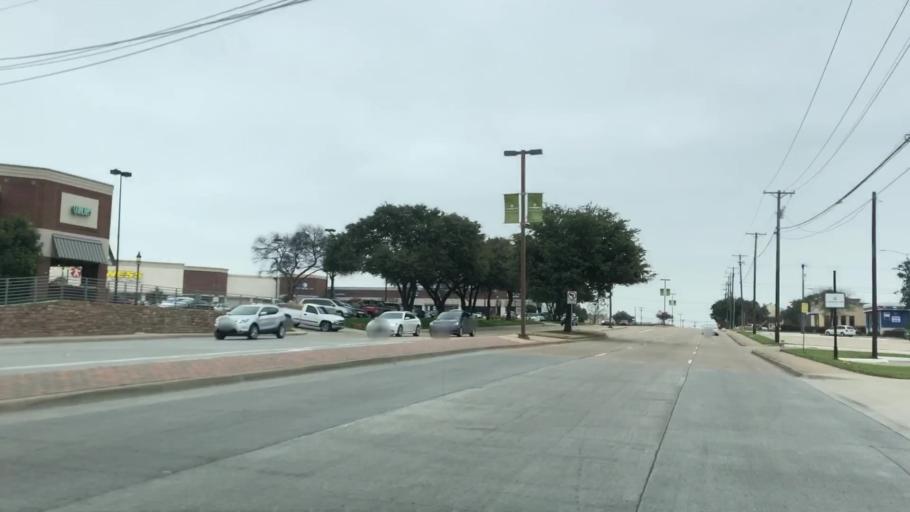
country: US
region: Texas
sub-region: Dallas County
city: Addison
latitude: 32.9867
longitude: -96.8549
